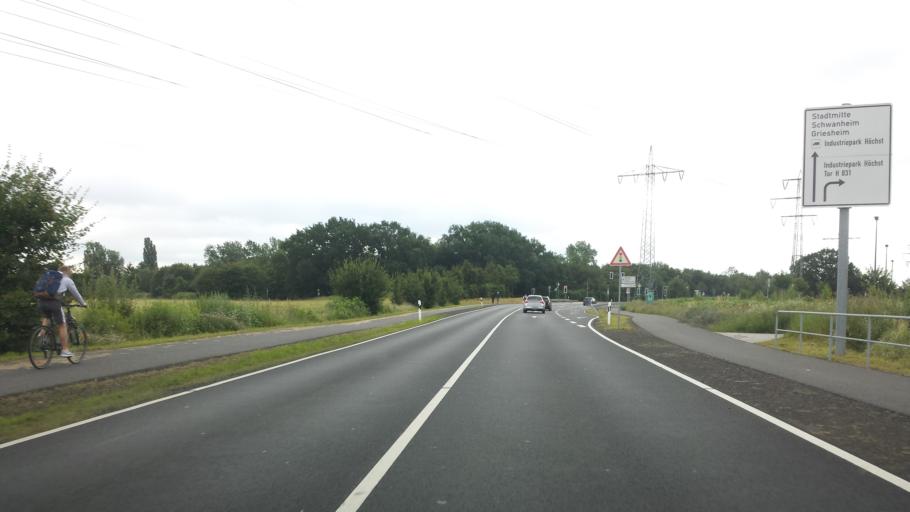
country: DE
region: Hesse
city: Kelsterbach
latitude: 50.0924
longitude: 8.5508
